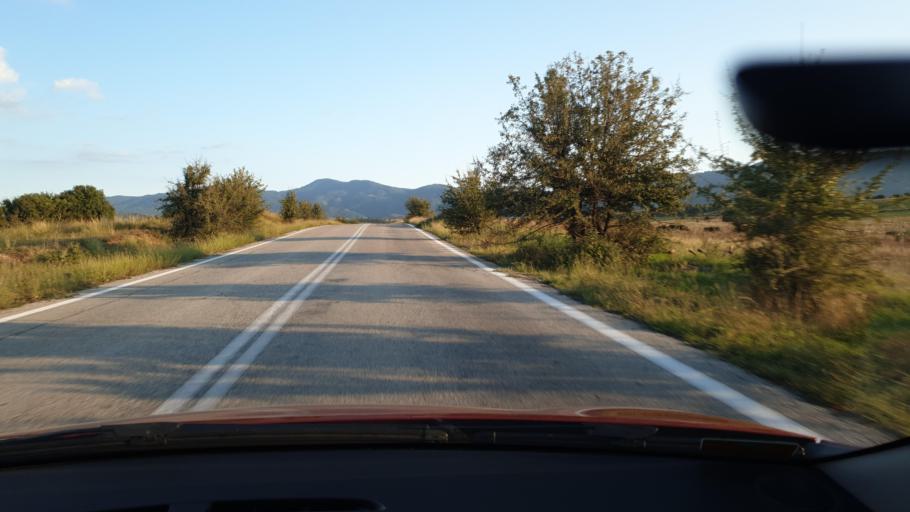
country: GR
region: Central Macedonia
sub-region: Nomos Thessalonikis
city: Nea Apollonia
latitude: 40.5346
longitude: 23.4695
